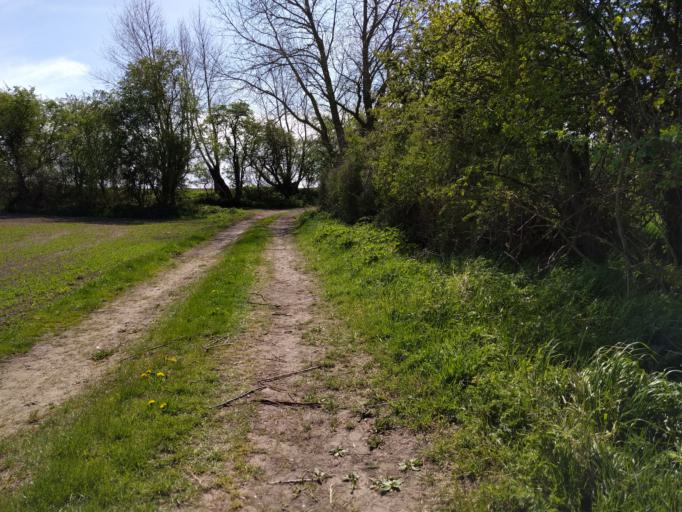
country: DK
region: South Denmark
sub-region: Kerteminde Kommune
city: Munkebo
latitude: 55.4540
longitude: 10.5908
